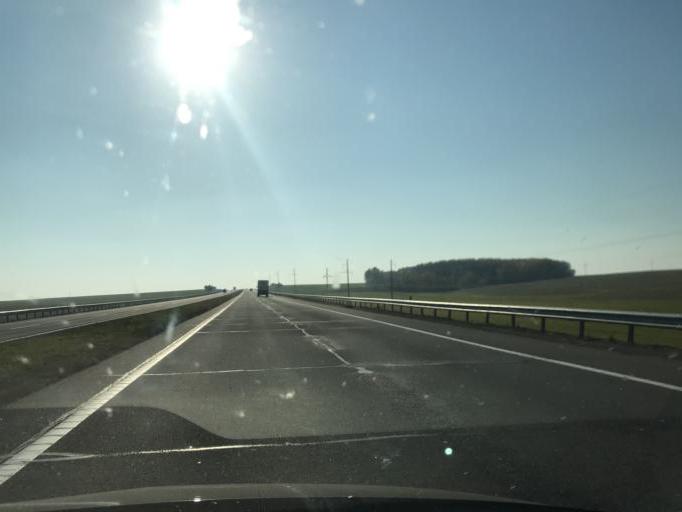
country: BY
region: Minsk
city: Novy Svyerzhan'
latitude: 53.4765
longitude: 26.6242
